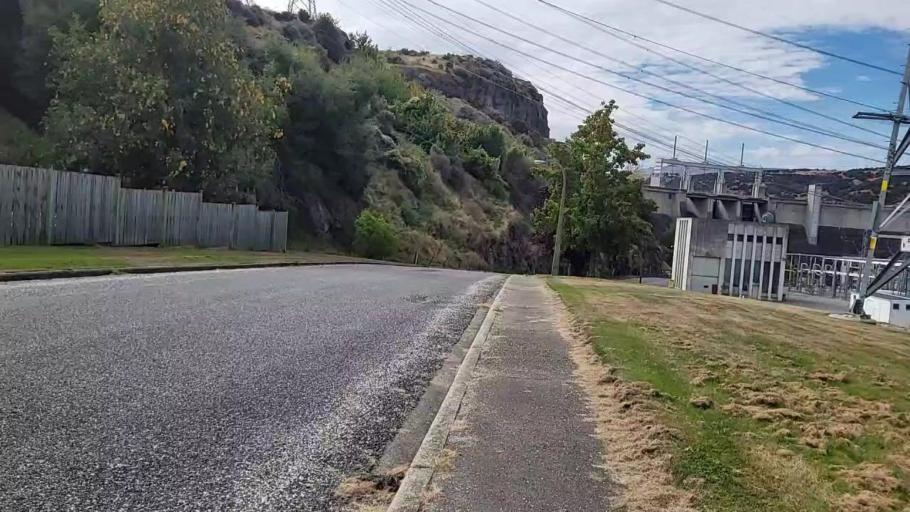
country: NZ
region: Otago
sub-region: Queenstown-Lakes District
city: Kingston
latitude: -45.4770
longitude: 169.3180
